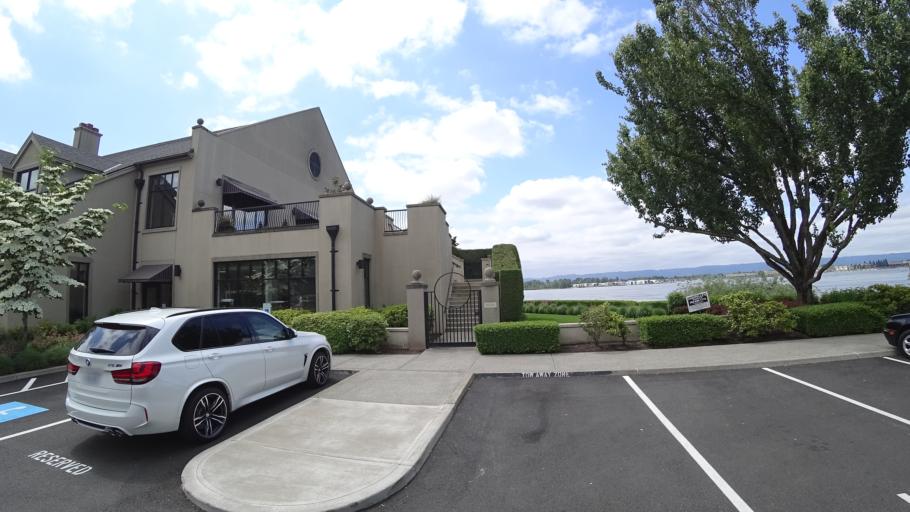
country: US
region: Washington
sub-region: Clark County
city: Vancouver
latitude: 45.6158
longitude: -122.6544
